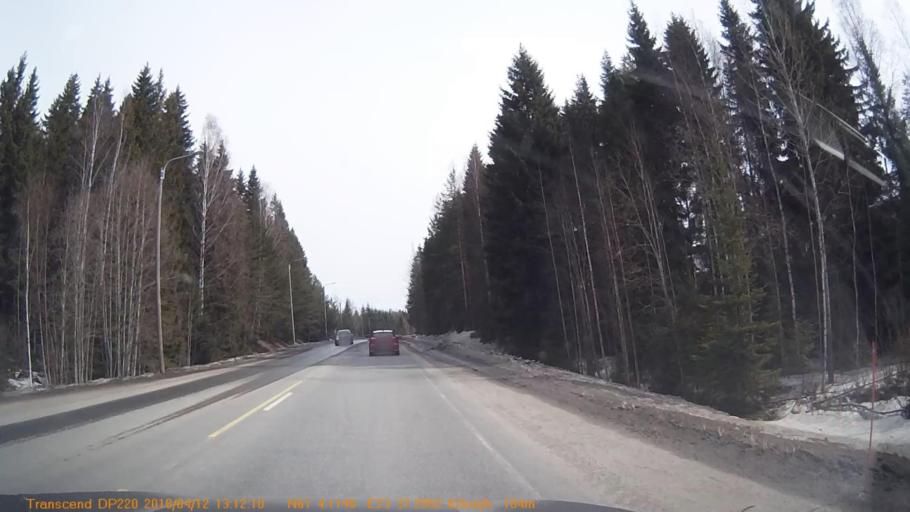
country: FI
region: Pirkanmaa
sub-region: Etelae-Pirkanmaa
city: Urjala
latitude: 61.0685
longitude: 23.6230
